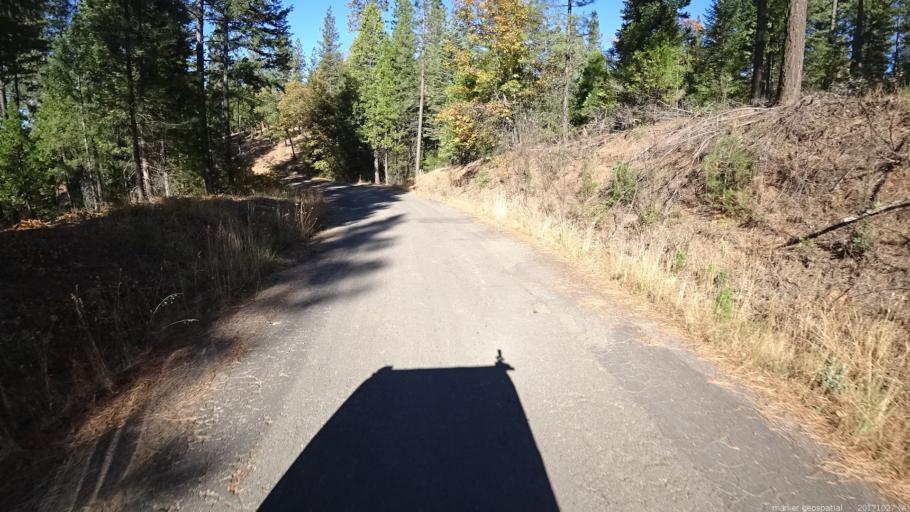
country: US
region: California
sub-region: Shasta County
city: Shingletown
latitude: 40.6208
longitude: -121.8365
